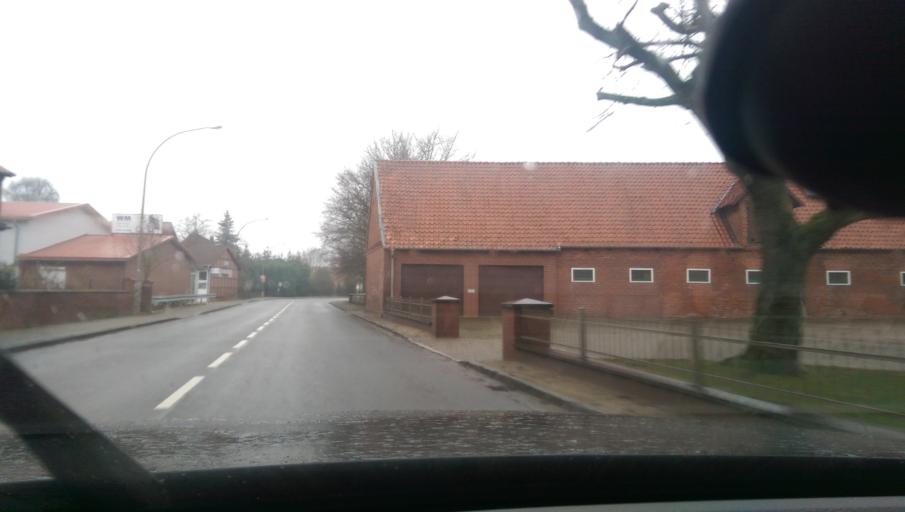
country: DE
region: Lower Saxony
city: Dorverden
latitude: 52.8558
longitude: 9.2356
